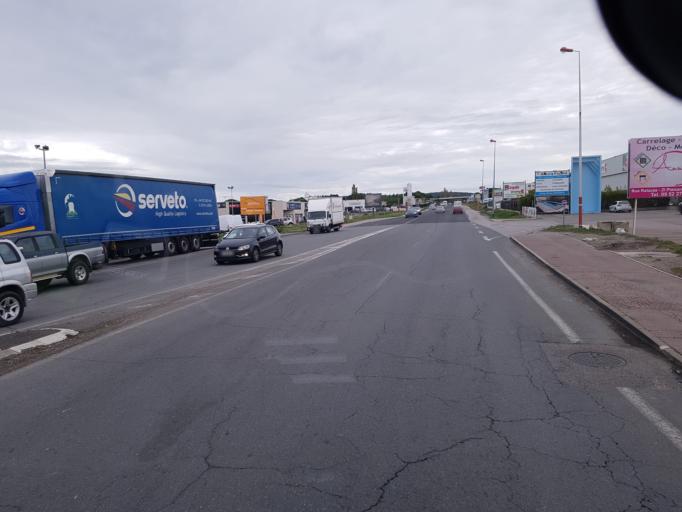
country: FR
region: Languedoc-Roussillon
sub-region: Departement de l'Aude
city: Narbonne
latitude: 43.1565
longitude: 2.9813
